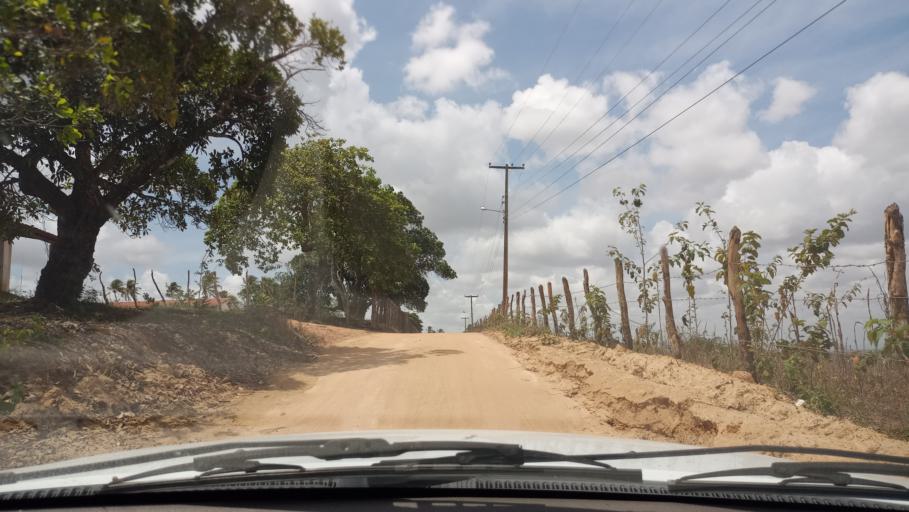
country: BR
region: Rio Grande do Norte
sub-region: Brejinho
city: Brejinho
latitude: -6.2570
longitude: -35.3392
